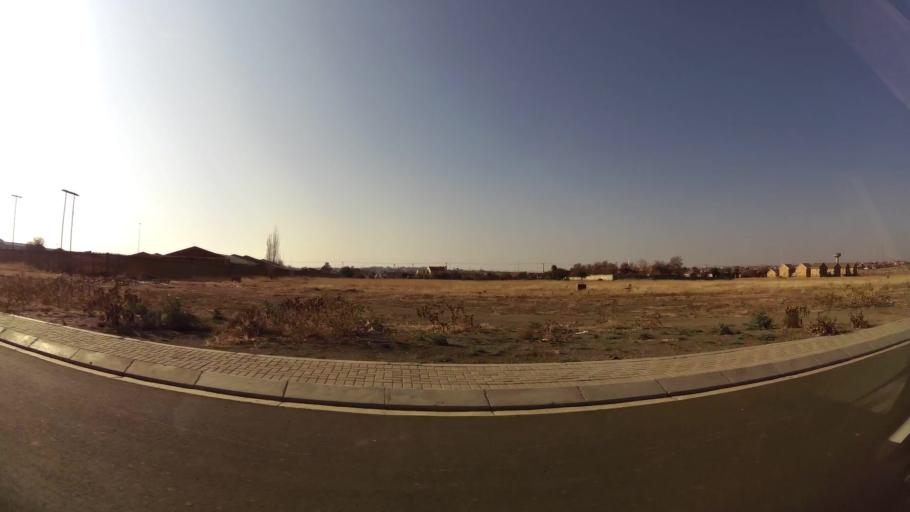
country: ZA
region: Orange Free State
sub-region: Mangaung Metropolitan Municipality
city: Bloemfontein
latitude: -29.1891
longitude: 26.2193
